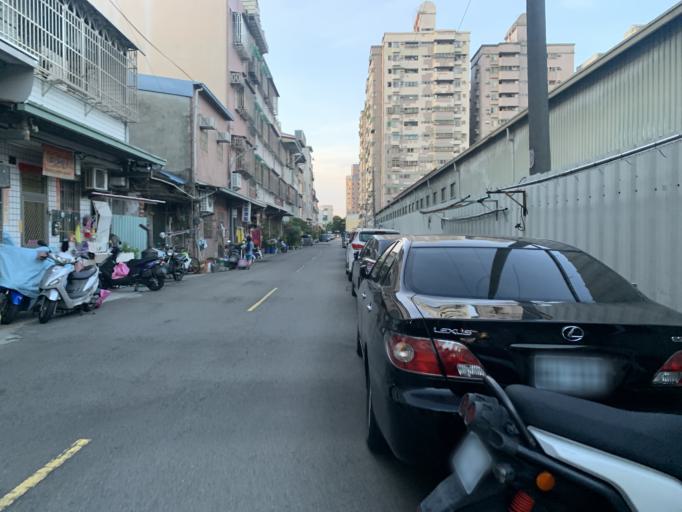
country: TW
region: Taiwan
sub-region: Taichung City
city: Taichung
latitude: 24.1506
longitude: 120.6146
